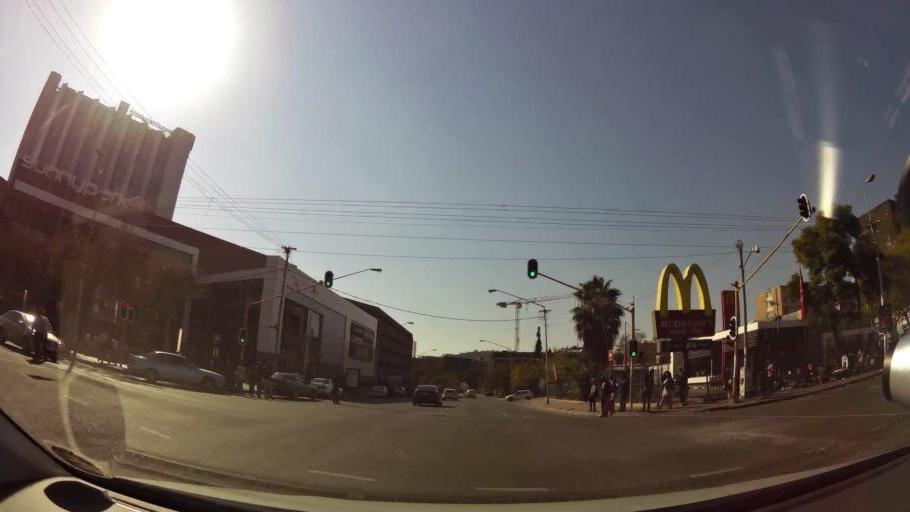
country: ZA
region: Gauteng
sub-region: City of Tshwane Metropolitan Municipality
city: Pretoria
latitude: -25.7517
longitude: 28.2035
